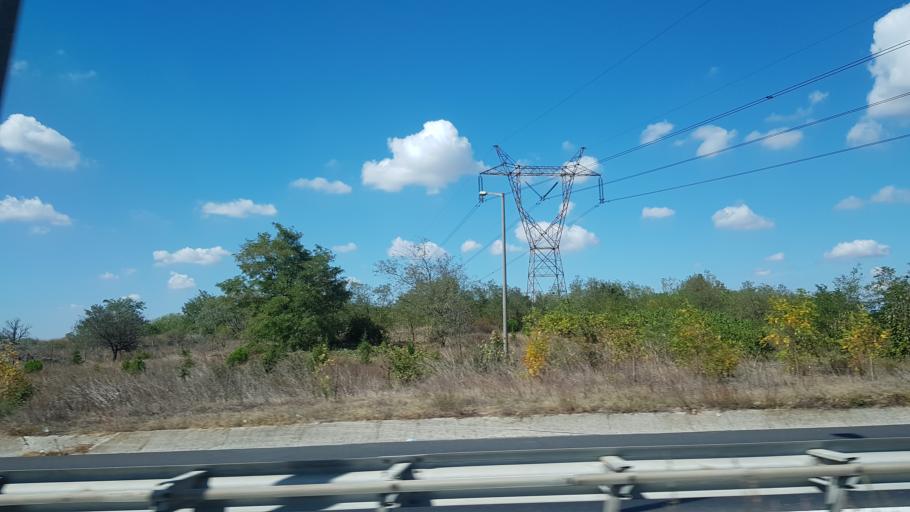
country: TR
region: Tekirdag
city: Velimese
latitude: 41.2282
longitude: 27.8759
